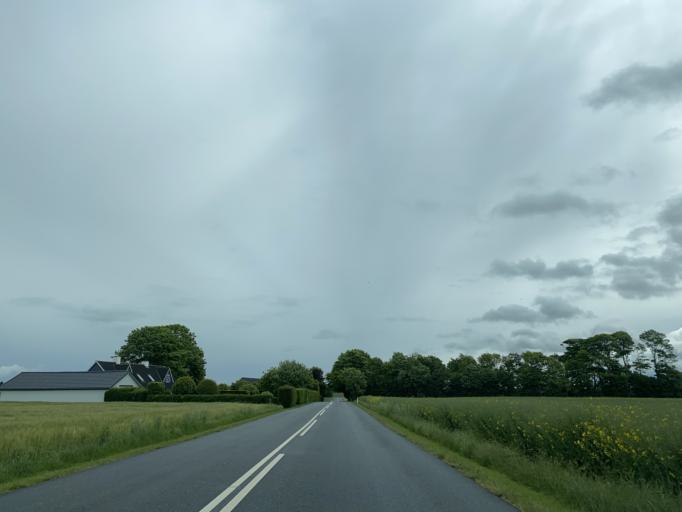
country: DK
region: Central Jutland
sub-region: Arhus Kommune
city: Sabro
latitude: 56.2499
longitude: 9.9997
